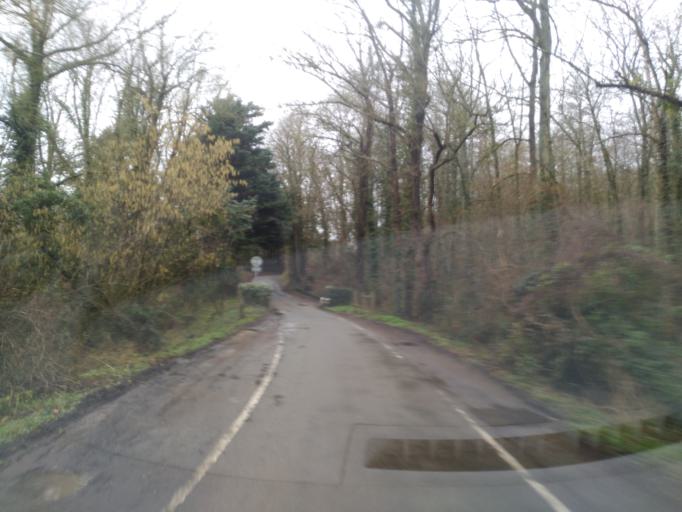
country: FR
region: Ile-de-France
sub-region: Departement des Yvelines
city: Chavenay
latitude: 48.8735
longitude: 2.0026
